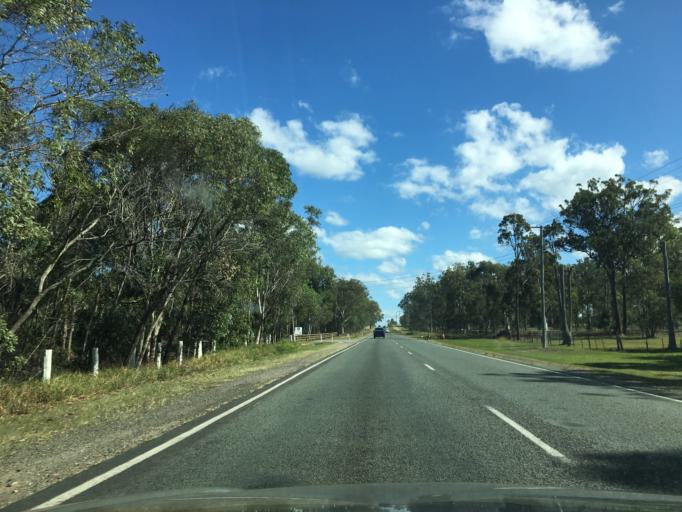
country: AU
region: Queensland
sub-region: Logan
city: Logan Reserve
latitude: -27.7364
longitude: 153.1281
